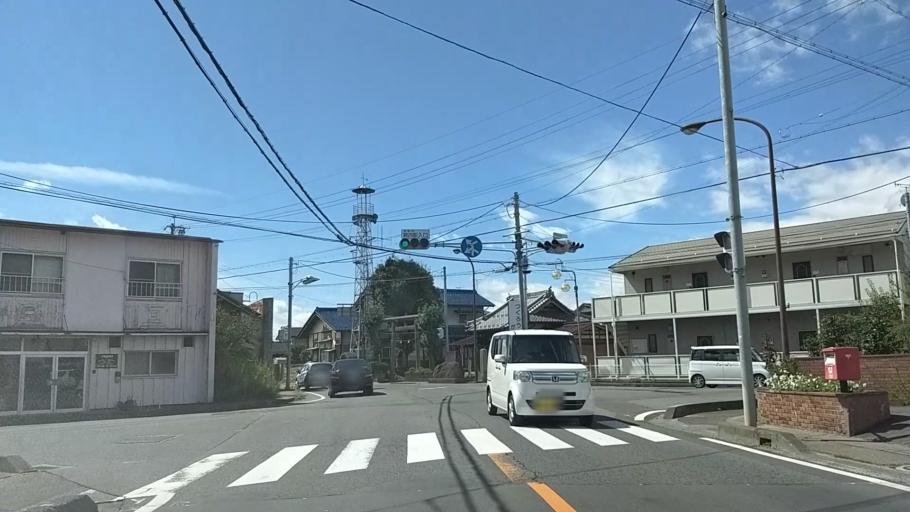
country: JP
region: Nagano
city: Suzaka
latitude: 36.6259
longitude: 138.2584
